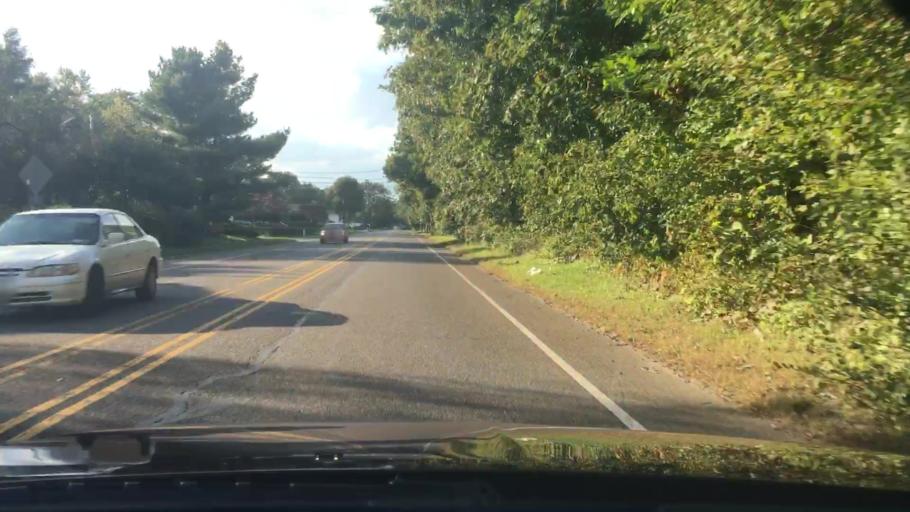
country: US
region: New York
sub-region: Suffolk County
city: Wheatley Heights
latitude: 40.7581
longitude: -73.3816
